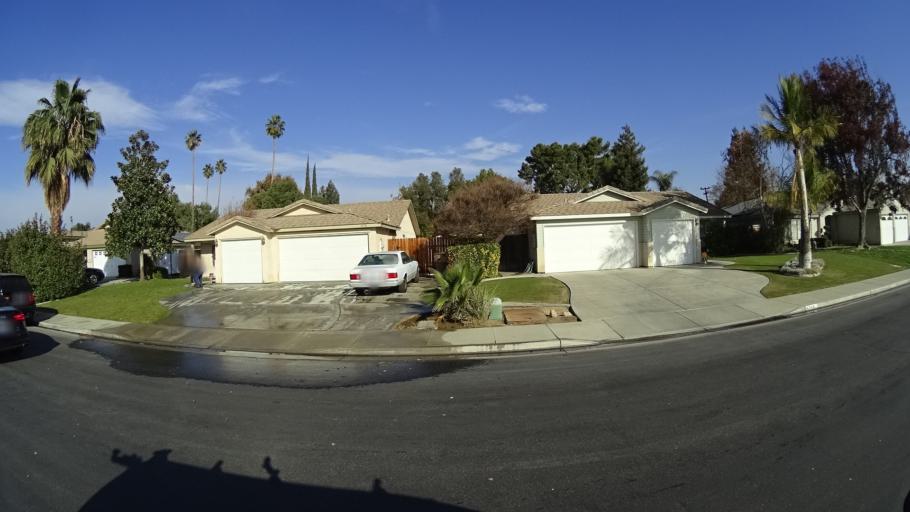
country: US
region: California
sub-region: Kern County
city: Oildale
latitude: 35.4081
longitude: -119.0660
